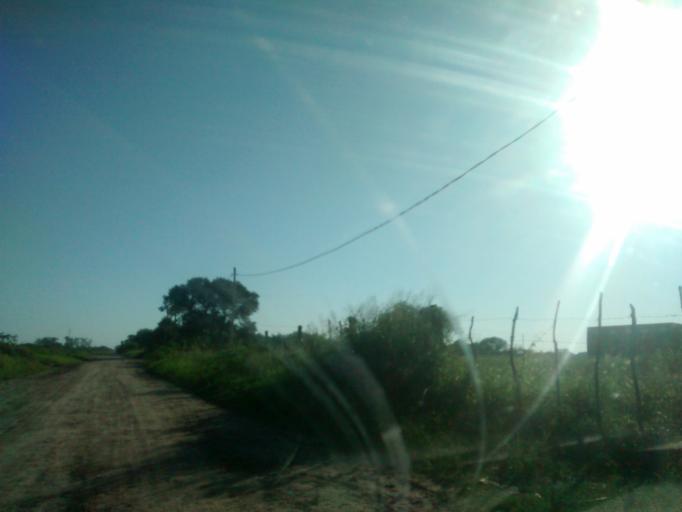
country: AR
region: Chaco
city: Resistencia
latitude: -27.4683
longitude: -59.0342
